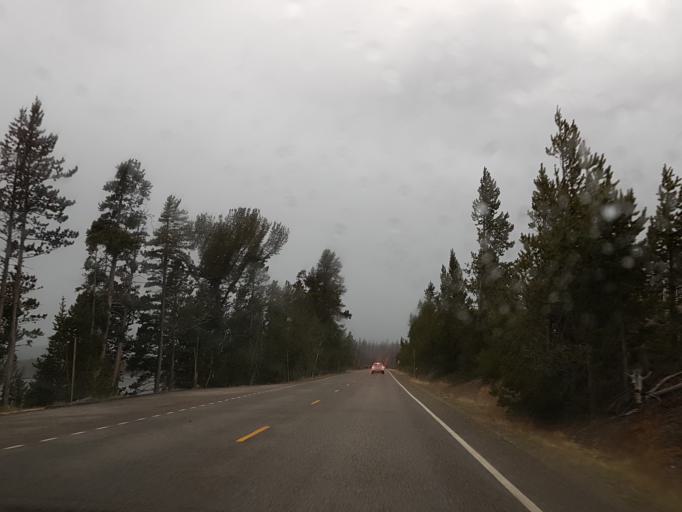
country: US
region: Montana
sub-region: Gallatin County
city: West Yellowstone
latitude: 44.4712
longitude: -110.5215
